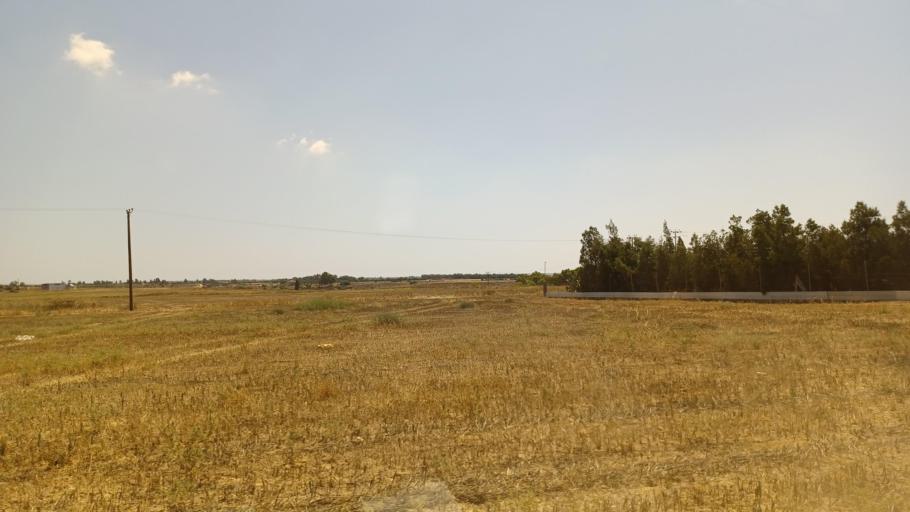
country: CY
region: Ammochostos
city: Achna
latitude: 35.0565
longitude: 33.8117
